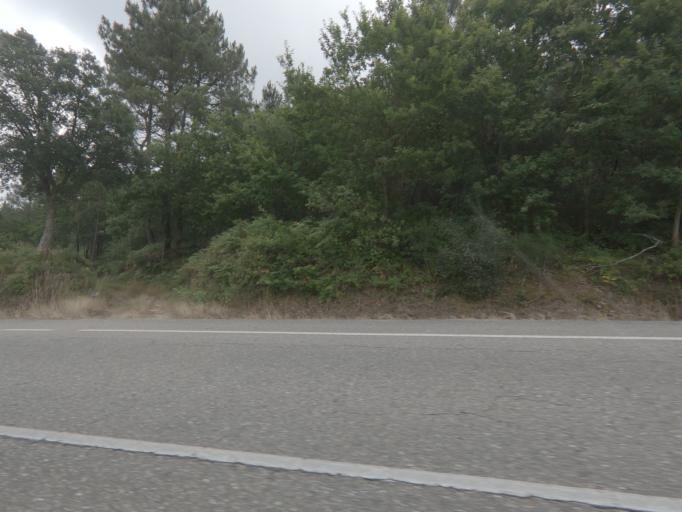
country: ES
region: Galicia
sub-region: Provincia de Pontevedra
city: O Rosal
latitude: 41.9337
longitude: -8.7934
